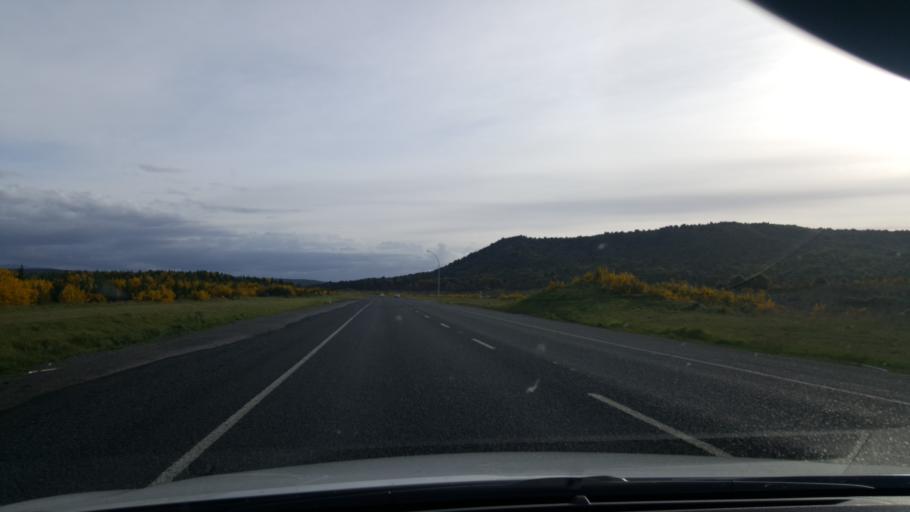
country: NZ
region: Waikato
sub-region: Taupo District
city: Taupo
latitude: -38.8416
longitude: 176.0617
